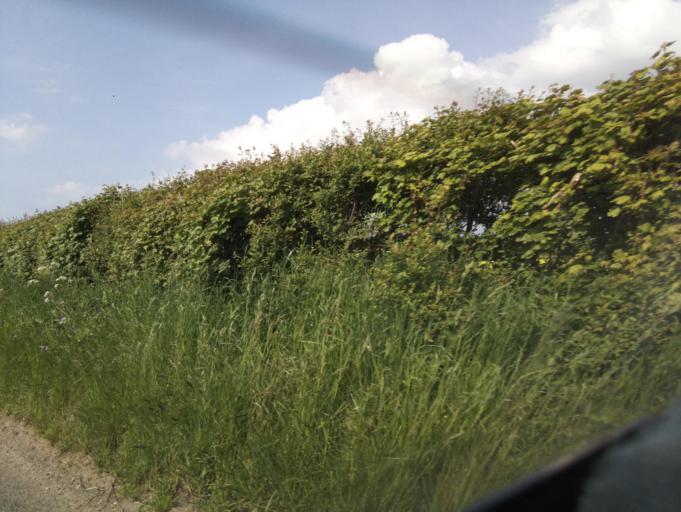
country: GB
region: England
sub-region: Wiltshire
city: Norton
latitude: 51.5501
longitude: -2.1528
